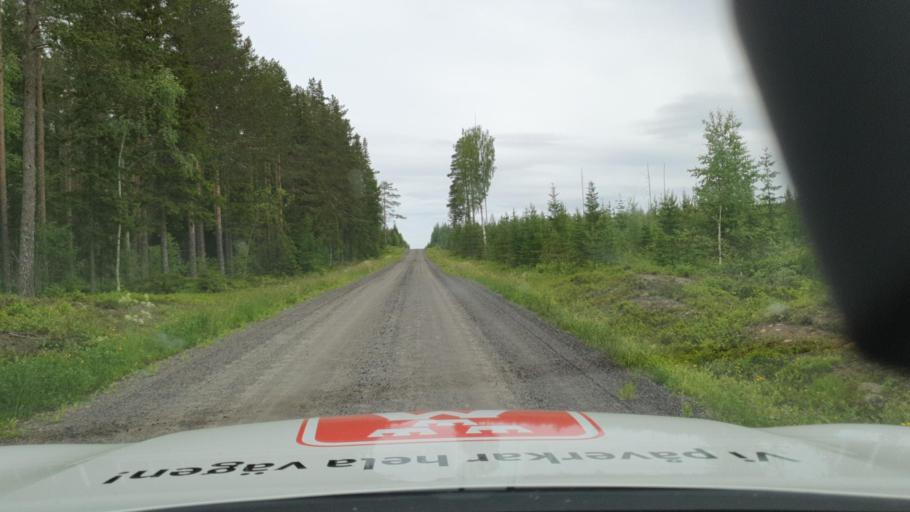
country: SE
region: Vaesterbotten
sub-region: Skelleftea Kommun
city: Burtraesk
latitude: 64.3666
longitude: 20.6168
